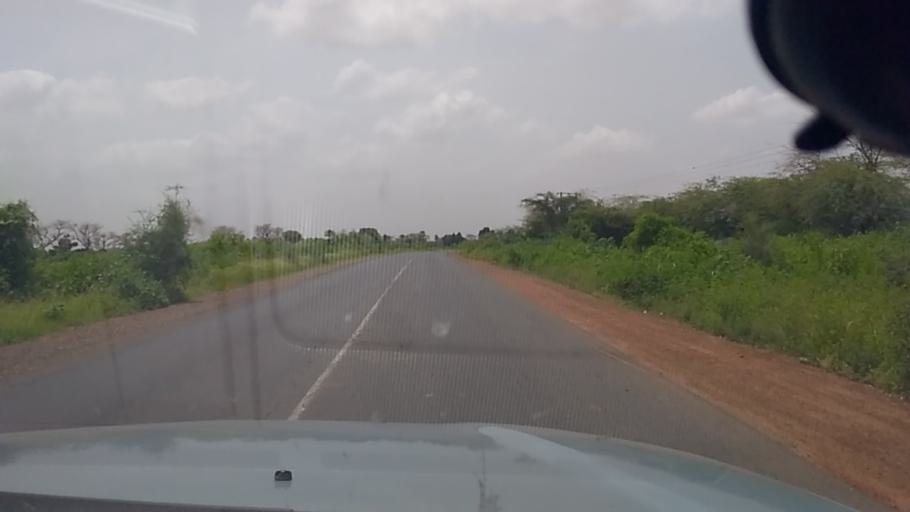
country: SN
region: Thies
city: Mekhe
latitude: 15.0287
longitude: -16.7242
